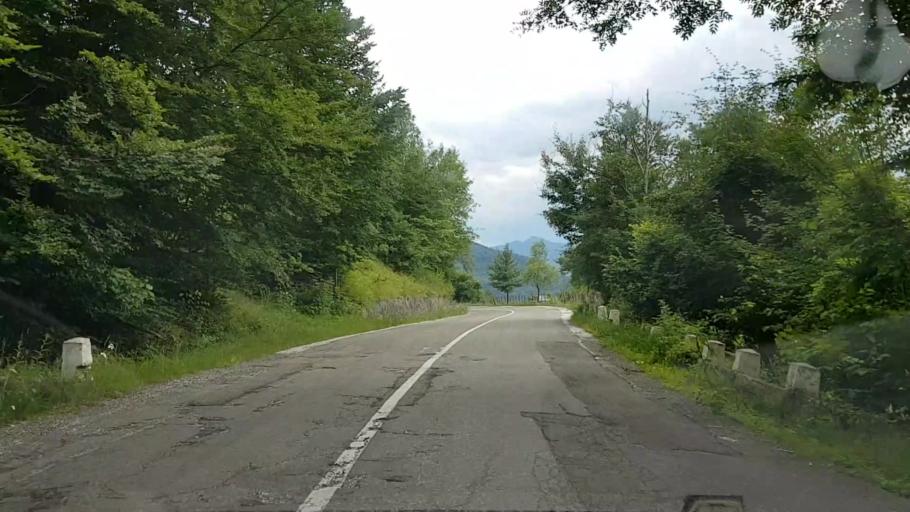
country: RO
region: Neamt
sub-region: Comuna Pangarati
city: Pangarati
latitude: 46.9618
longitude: 26.1227
